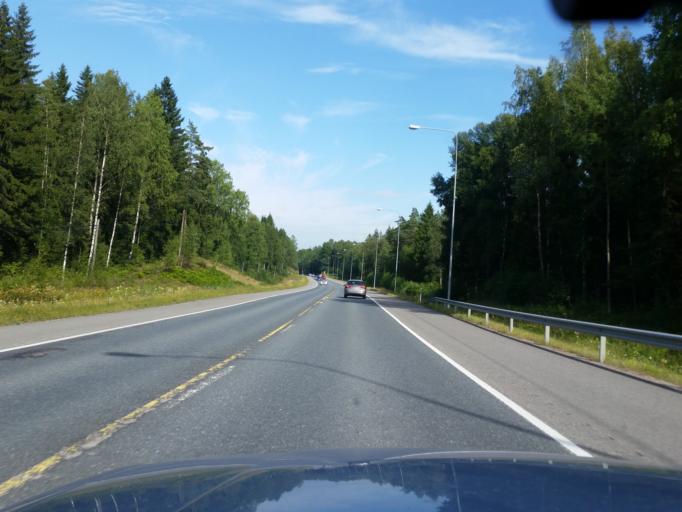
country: FI
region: Uusimaa
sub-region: Helsinki
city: Siuntio
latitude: 60.0964
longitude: 24.2738
